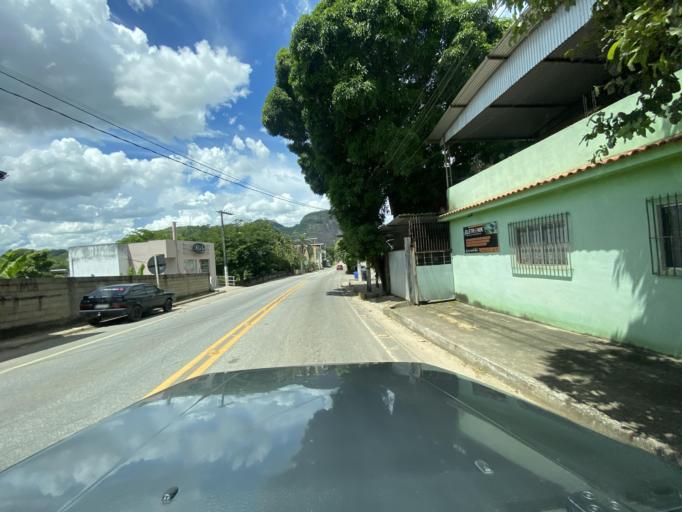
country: BR
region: Espirito Santo
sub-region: Jeronimo Monteiro
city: Jeronimo Monteiro
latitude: -20.7903
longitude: -41.3915
